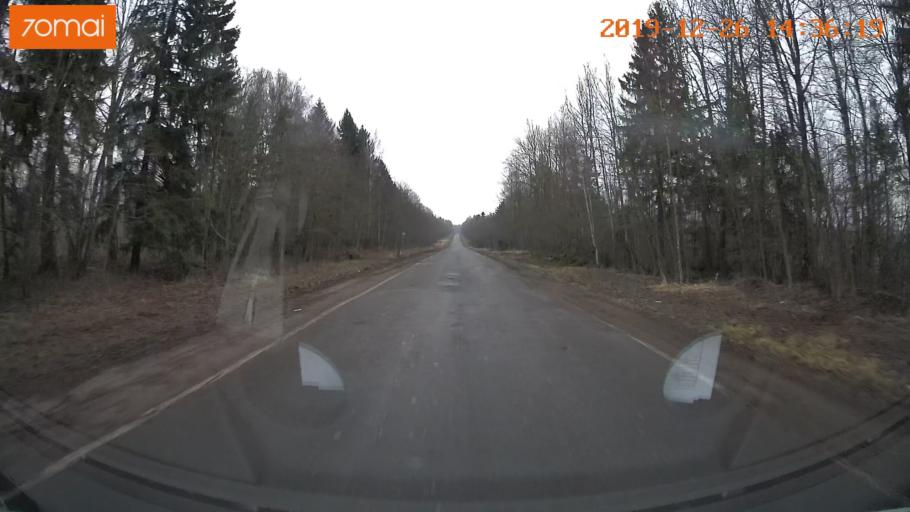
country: RU
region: Jaroslavl
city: Poshekhon'ye
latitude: 58.4125
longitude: 38.9766
